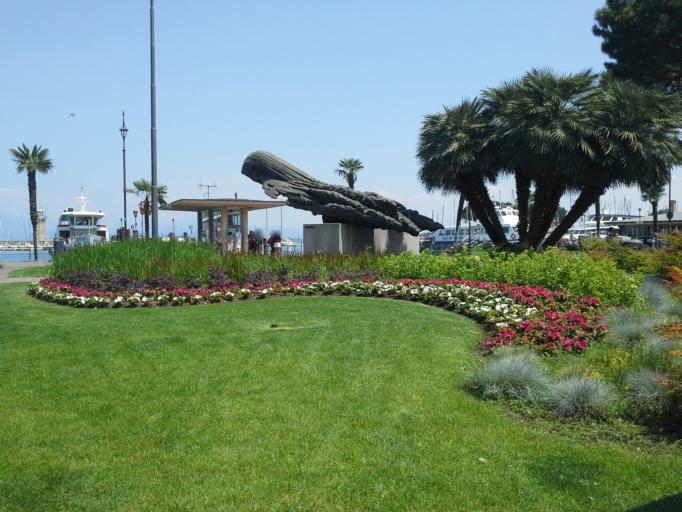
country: IT
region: Lombardy
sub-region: Provincia di Brescia
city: Desenzano del Garda
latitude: 45.4698
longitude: 10.5407
